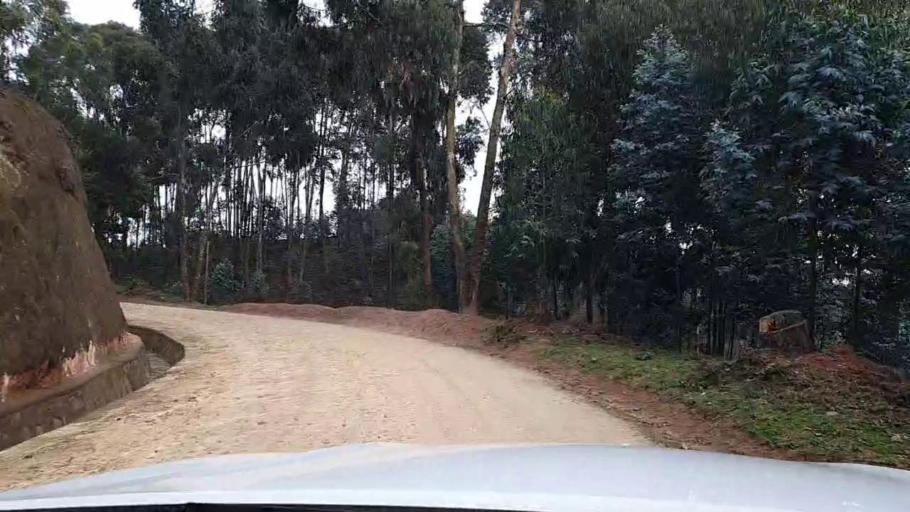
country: RW
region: Southern Province
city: Nzega
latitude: -2.3809
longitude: 29.3834
